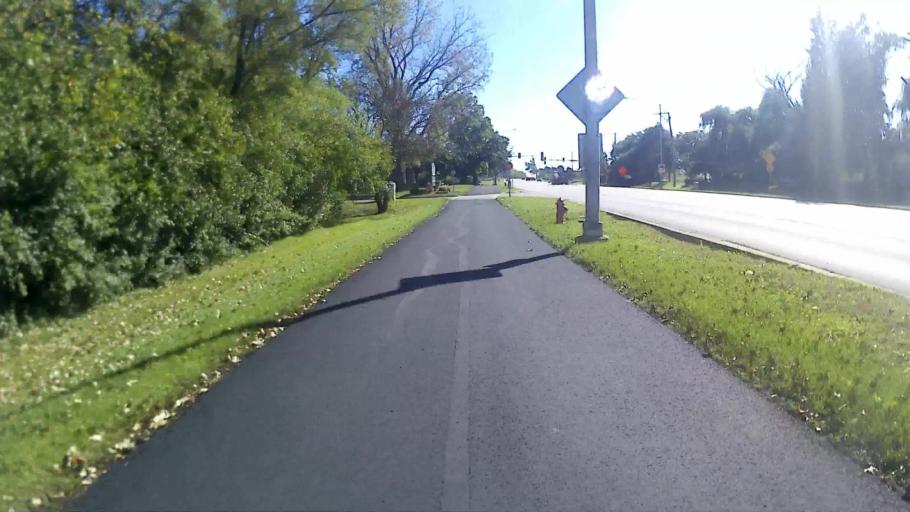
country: US
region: Illinois
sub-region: DuPage County
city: Wood Dale
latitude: 41.9533
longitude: -87.9889
